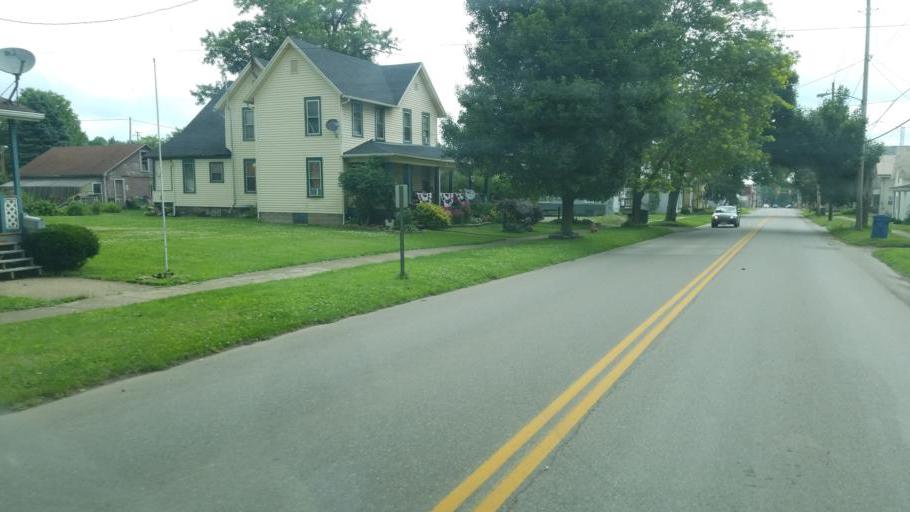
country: US
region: Ohio
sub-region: Columbiana County
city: Lisbon
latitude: 40.7710
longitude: -80.7716
